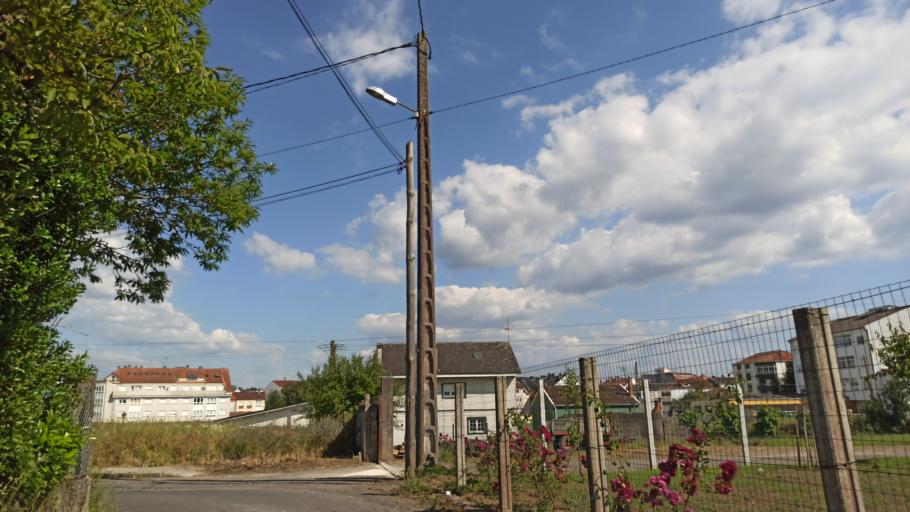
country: ES
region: Galicia
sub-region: Provincia da Coruna
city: Negreira
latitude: 42.9139
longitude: -8.7387
